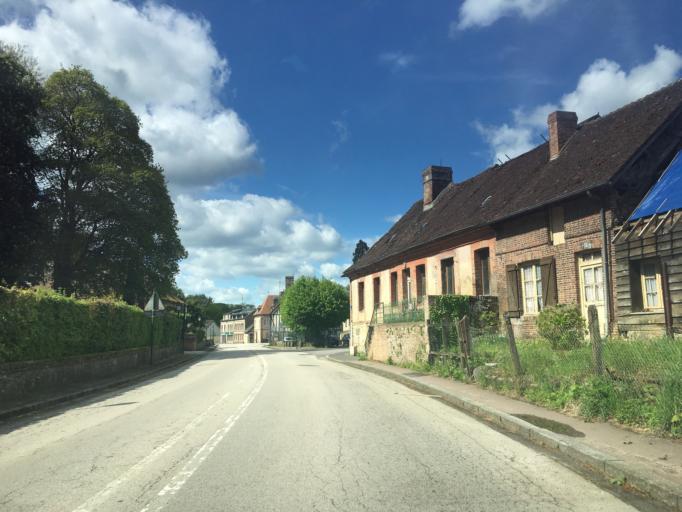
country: FR
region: Lower Normandy
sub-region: Departement de l'Orne
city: Aube-sur-Rile
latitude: 48.8409
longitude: 0.5135
